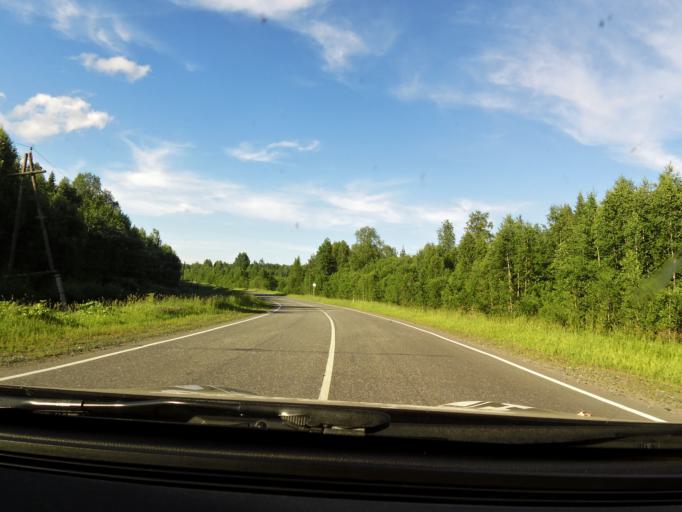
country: RU
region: Kirov
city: Lesnyye Polyany
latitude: 58.8023
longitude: 52.5842
